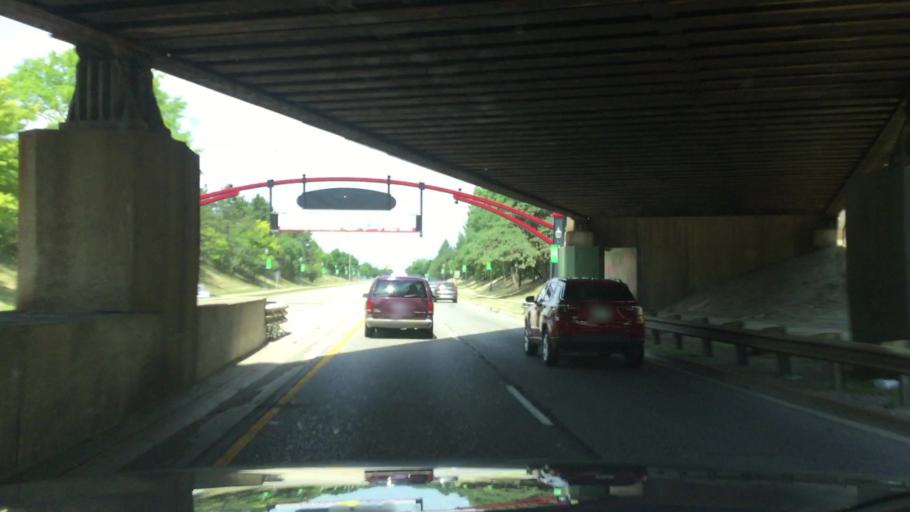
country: US
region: Michigan
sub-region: Genesee County
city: Grand Blanc
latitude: 42.9325
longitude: -83.6360
